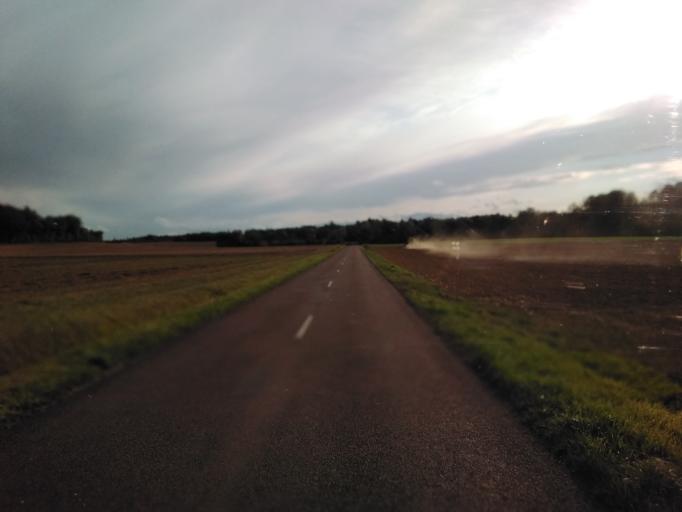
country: FR
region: Champagne-Ardenne
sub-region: Departement de l'Aube
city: Les Riceys
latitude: 47.8858
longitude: 4.3587
